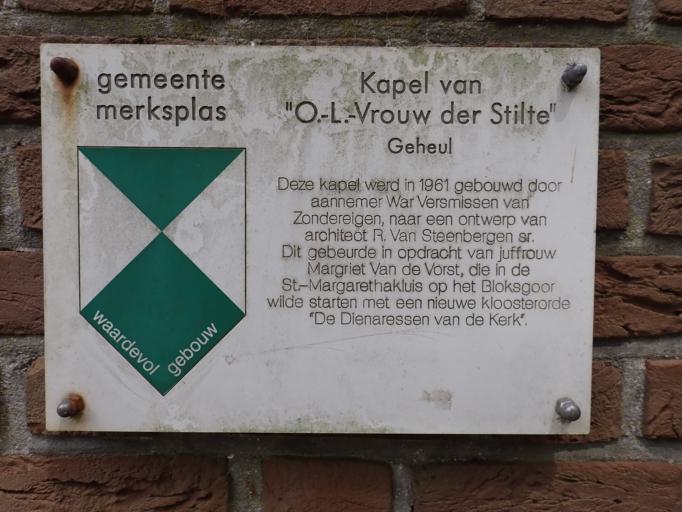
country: BE
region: Flanders
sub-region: Provincie Antwerpen
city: Baarle-Hertog
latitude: 51.3834
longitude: 4.8994
